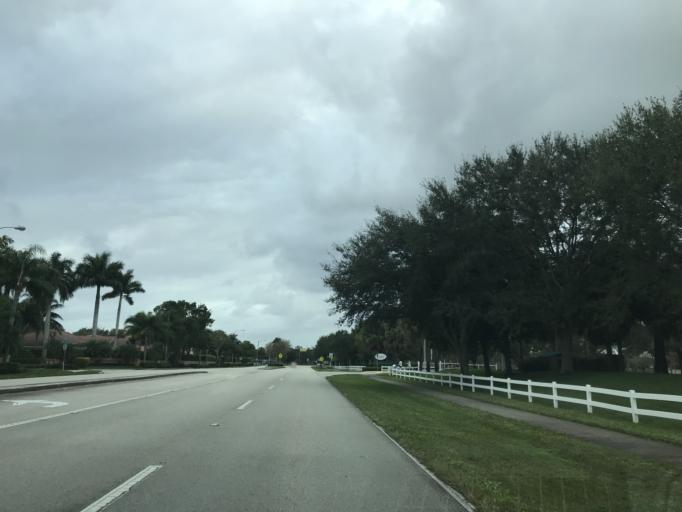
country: US
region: Florida
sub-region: Broward County
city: Coral Springs
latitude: 26.2981
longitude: -80.2639
